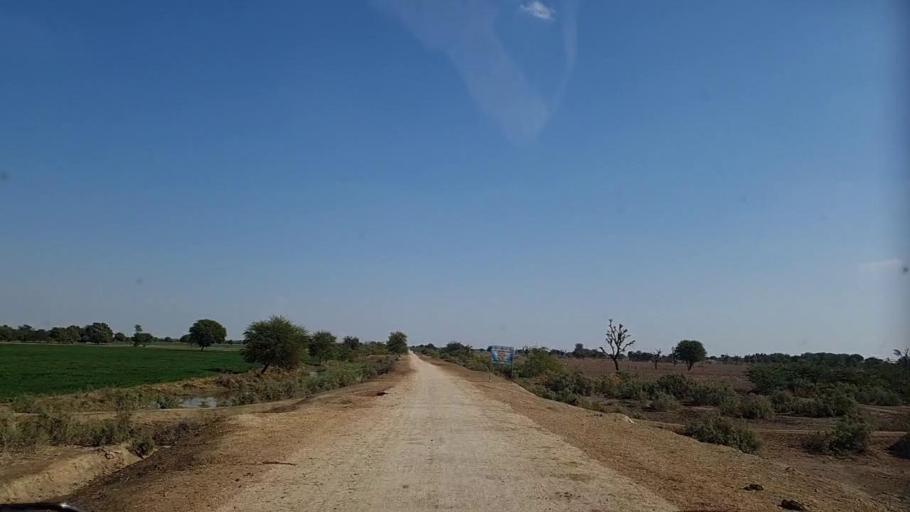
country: PK
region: Sindh
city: Pithoro
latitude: 25.6864
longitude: 69.4495
